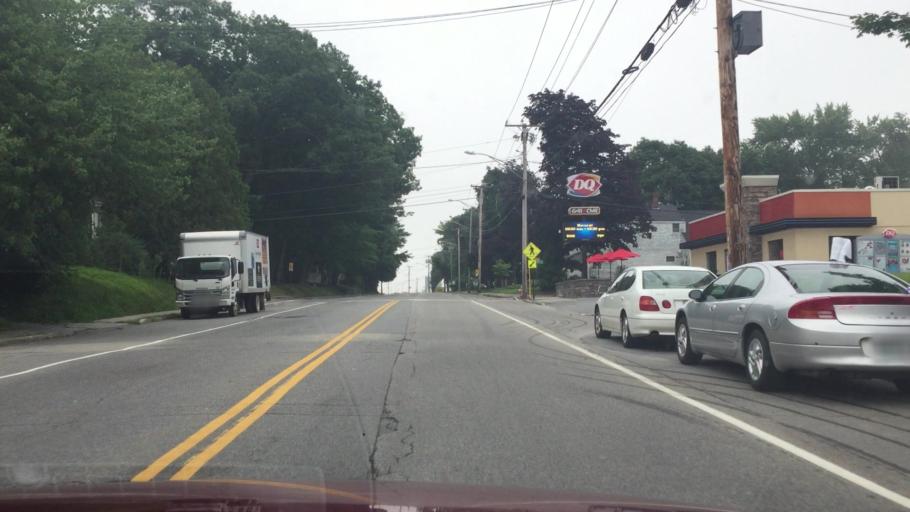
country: US
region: Maine
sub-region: Cumberland County
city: Westbrook
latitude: 43.6796
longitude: -70.3420
